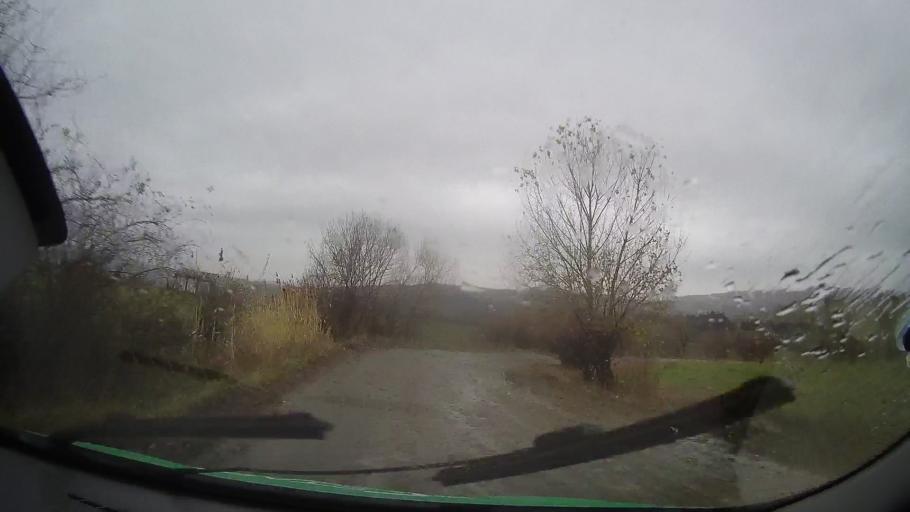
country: RO
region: Bistrita-Nasaud
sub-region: Comuna Monor
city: Monor
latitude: 46.9485
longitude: 24.7137
